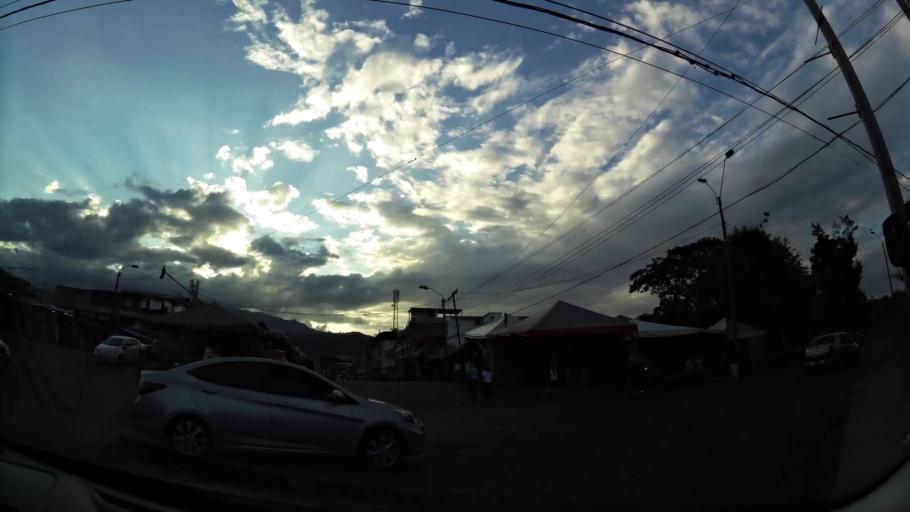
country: CO
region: Valle del Cauca
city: Cali
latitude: 3.4292
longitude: -76.5199
